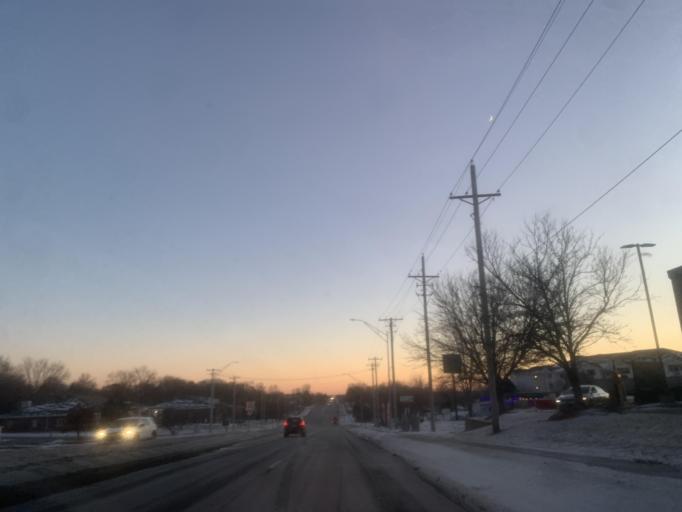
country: US
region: Nebraska
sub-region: Douglas County
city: Ralston
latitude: 41.2045
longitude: -96.0815
